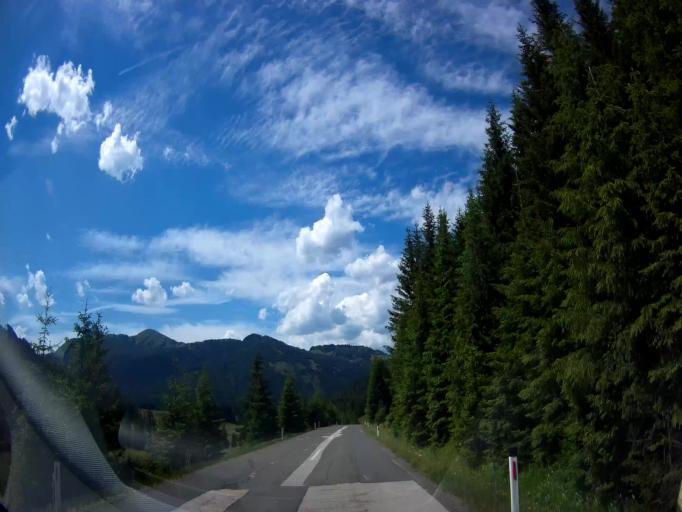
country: AT
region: Styria
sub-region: Politischer Bezirk Murau
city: Stadl an der Mur
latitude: 46.9653
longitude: 14.0207
